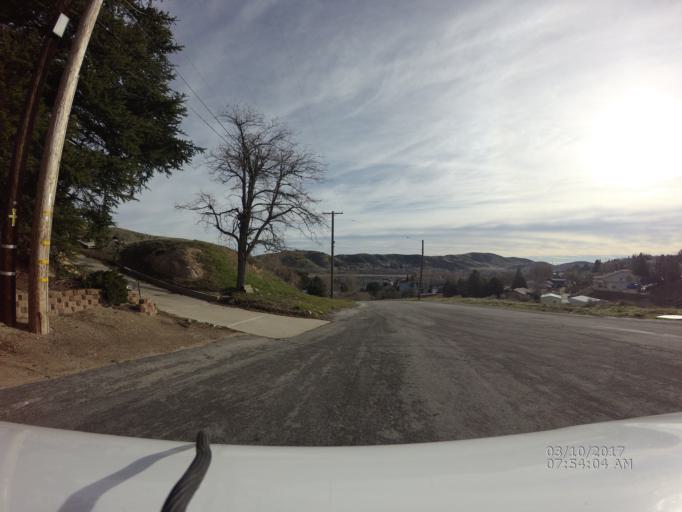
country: US
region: California
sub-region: Los Angeles County
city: Green Valley
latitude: 34.6625
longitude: -118.4032
